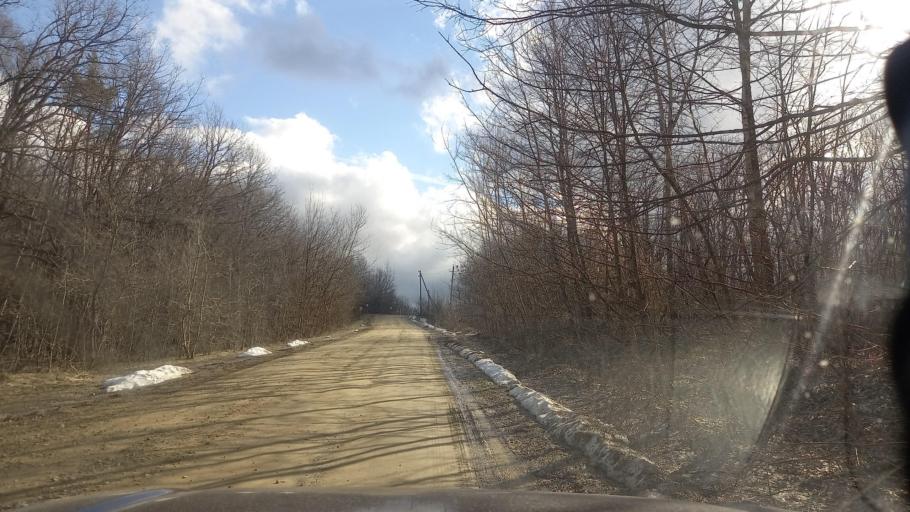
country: RU
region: Krasnodarskiy
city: Smolenskaya
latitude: 44.5791
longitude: 38.8081
